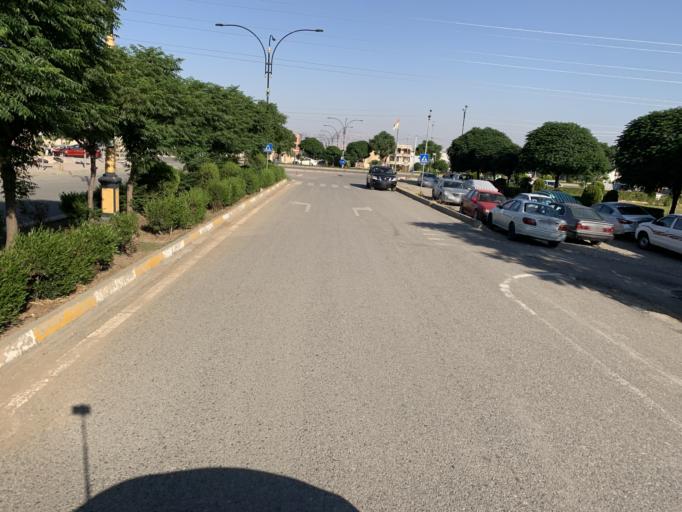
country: IQ
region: As Sulaymaniyah
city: Raniye
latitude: 36.2411
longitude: 44.8746
